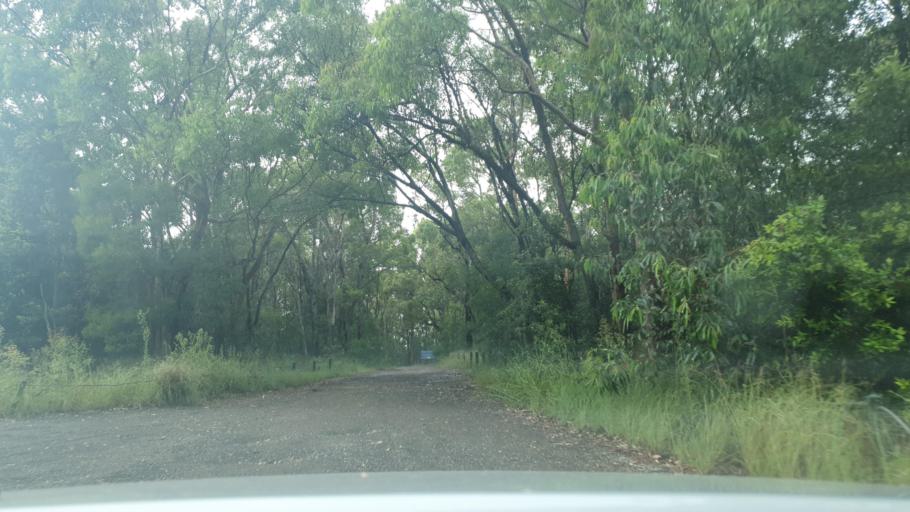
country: AU
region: New South Wales
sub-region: Blue Mountains Municipality
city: Glenbrook
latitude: -33.7785
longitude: 150.6277
